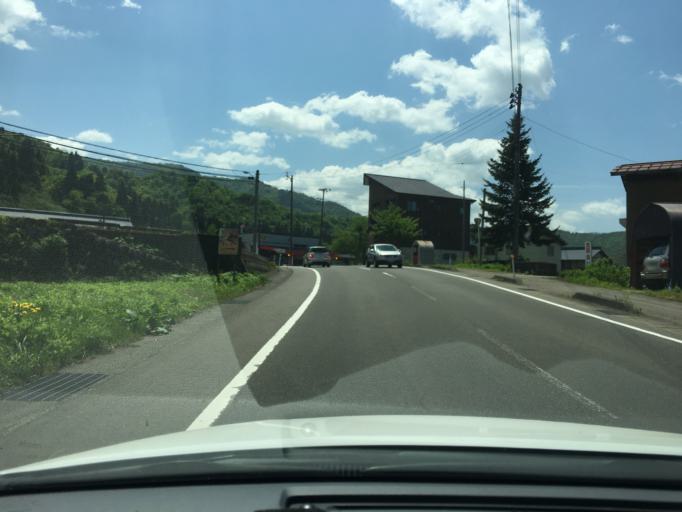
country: JP
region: Niigata
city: Tochio-honcho
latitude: 37.3482
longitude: 139.0495
